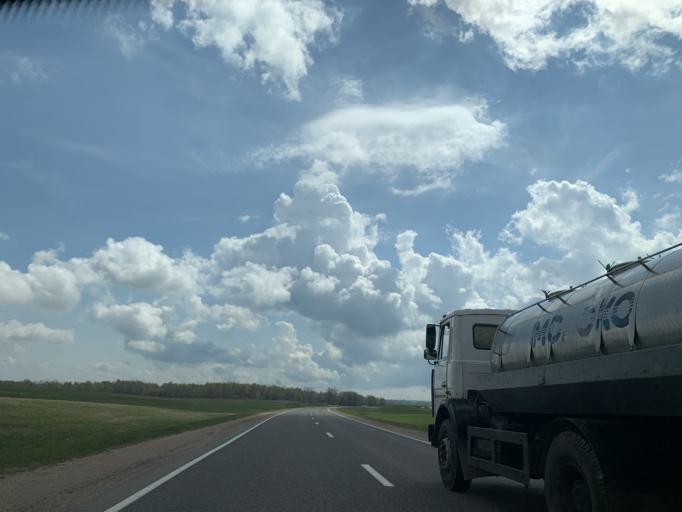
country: BY
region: Minsk
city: Nyasvizh
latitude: 53.2499
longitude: 26.6917
